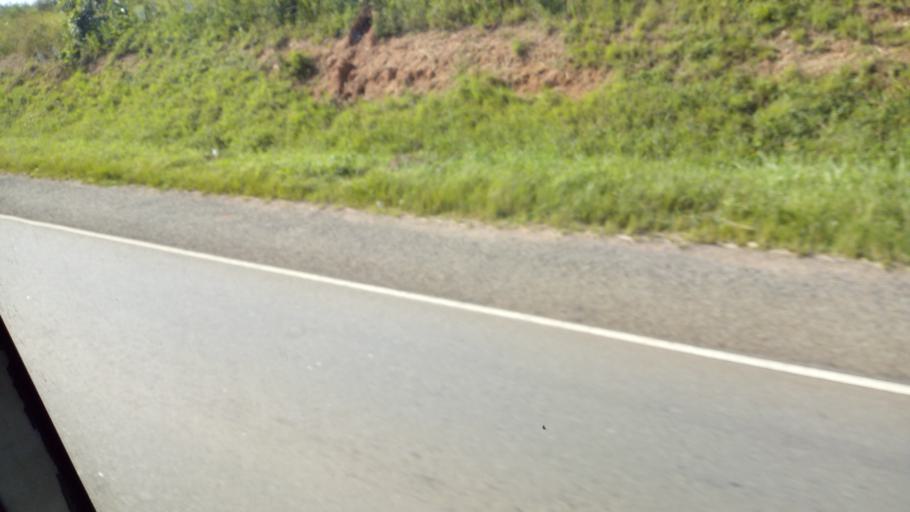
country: UG
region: Central Region
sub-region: Lyantonde District
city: Lyantonde
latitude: -0.4389
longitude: 31.0826
